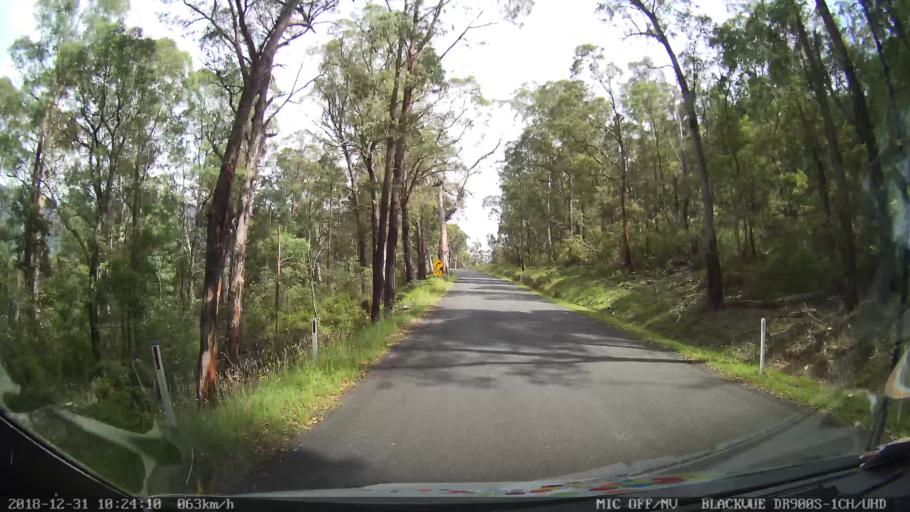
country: AU
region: New South Wales
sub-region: Snowy River
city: Jindabyne
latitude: -36.5143
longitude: 148.1406
